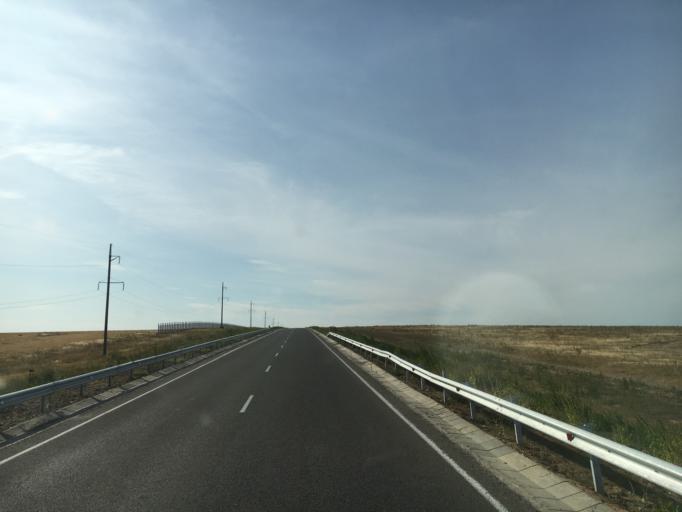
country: KZ
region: Batys Qazaqstan
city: Kamenka
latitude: 51.1431
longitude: 50.1002
